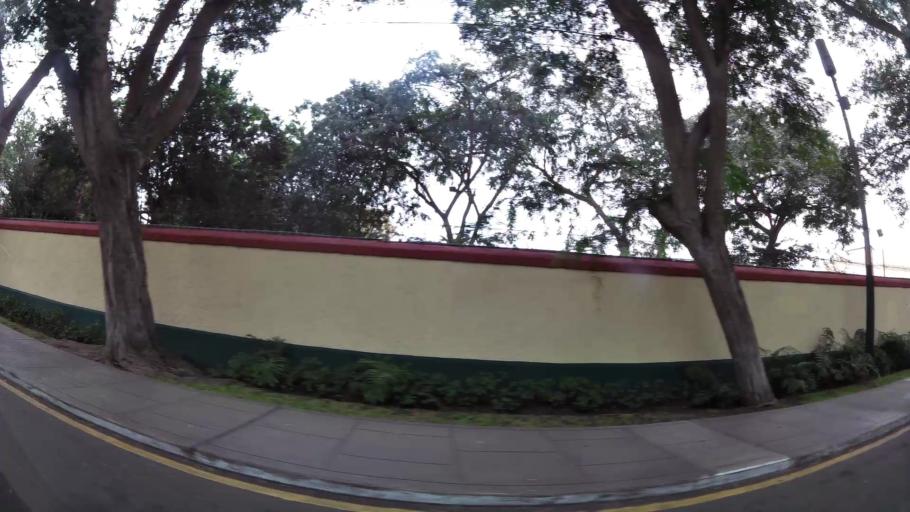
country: PE
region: Lima
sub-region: Lima
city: San Isidro
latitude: -12.0973
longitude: -77.0387
